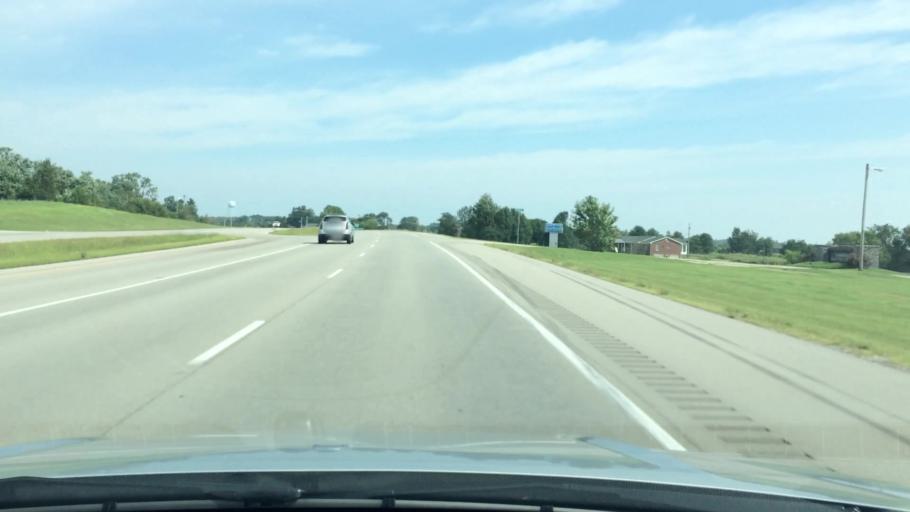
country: US
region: Kentucky
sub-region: Anderson County
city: Lawrenceburg
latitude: 38.1063
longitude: -84.9155
